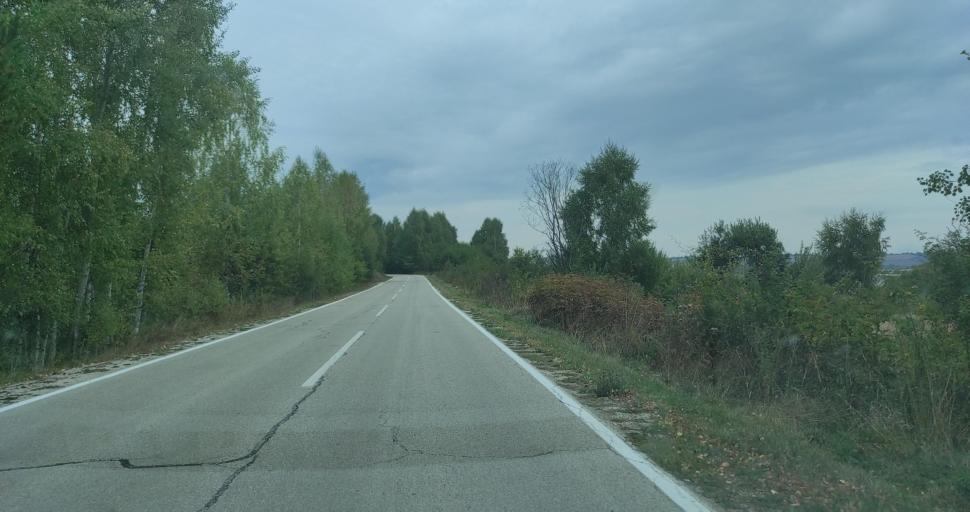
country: RS
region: Central Serbia
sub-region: Jablanicki Okrug
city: Crna Trava
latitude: 42.7192
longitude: 22.3329
